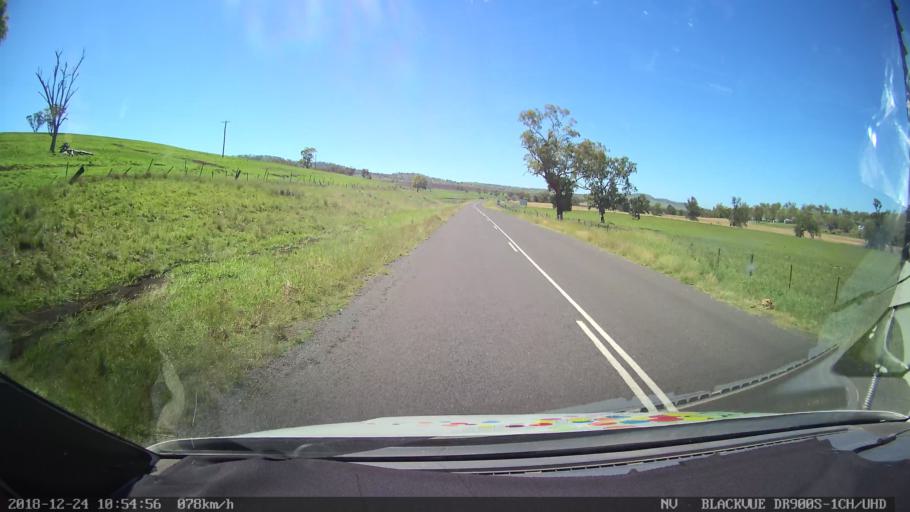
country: AU
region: New South Wales
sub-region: Upper Hunter Shire
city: Merriwa
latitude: -32.0103
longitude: 150.4173
